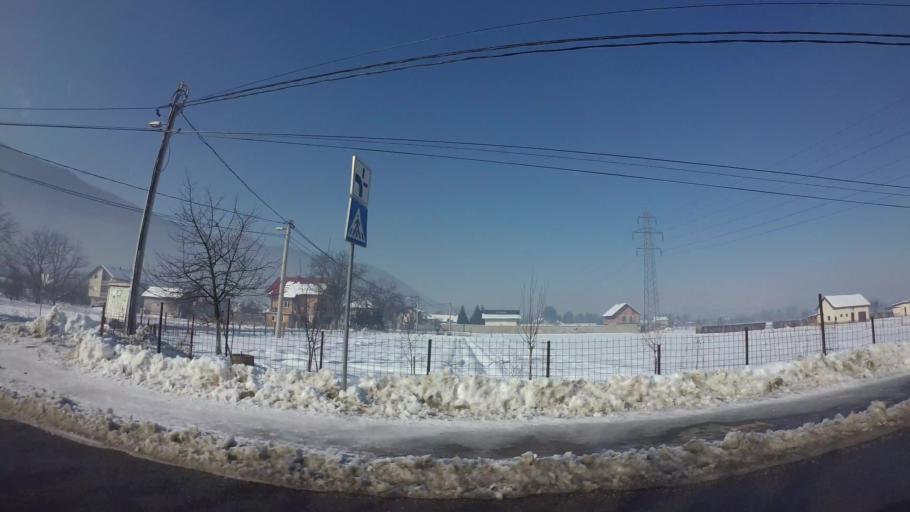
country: BA
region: Federation of Bosnia and Herzegovina
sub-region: Kanton Sarajevo
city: Sarajevo
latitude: 43.8087
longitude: 18.2994
